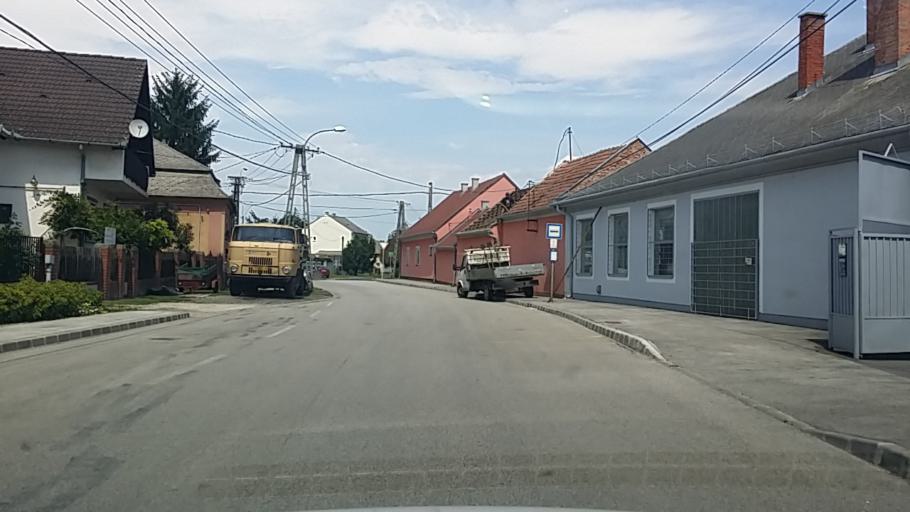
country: HU
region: Zala
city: Nagykanizsa
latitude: 46.4525
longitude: 16.9651
